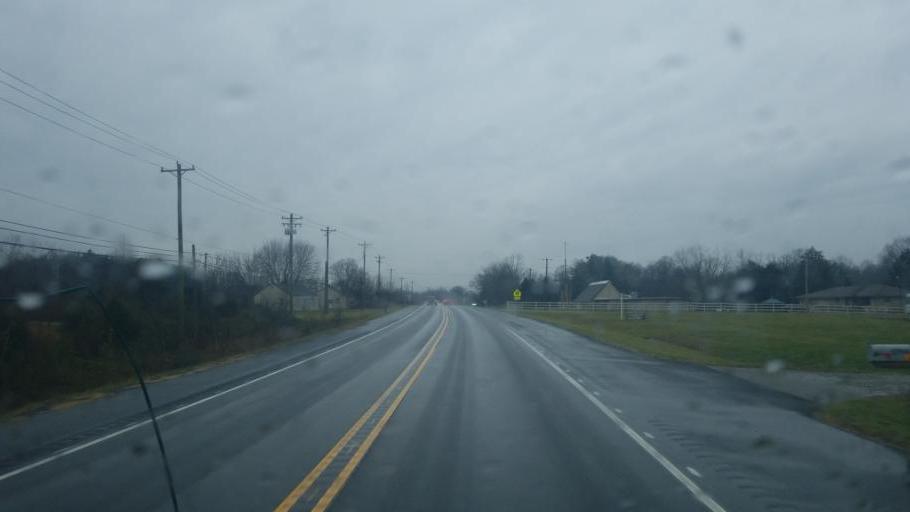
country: US
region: Indiana
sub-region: Bartholomew County
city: Columbus
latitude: 39.1988
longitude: -85.9861
